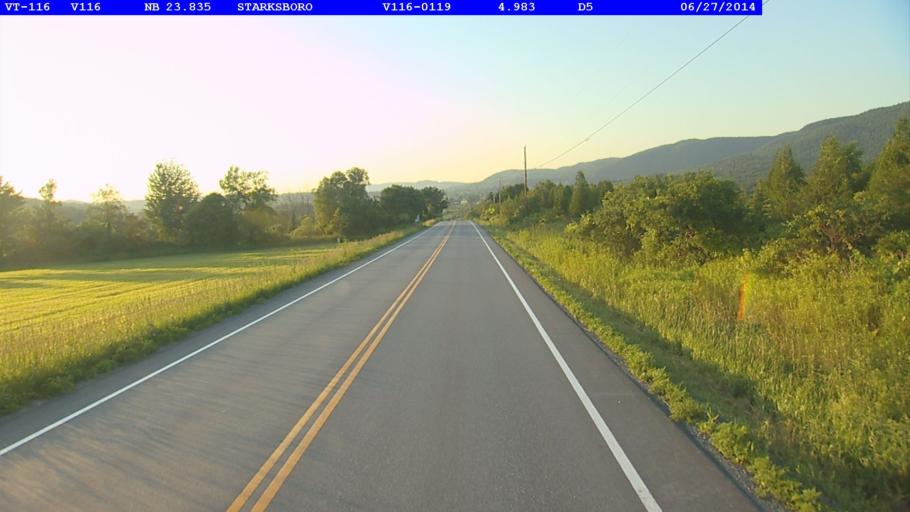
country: US
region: Vermont
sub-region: Chittenden County
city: Hinesburg
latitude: 44.2560
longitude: -73.0635
